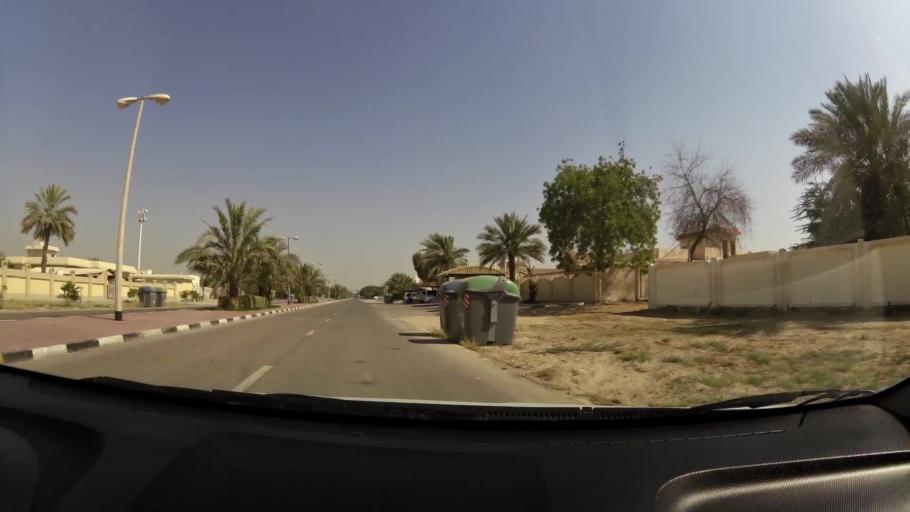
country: AE
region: Ajman
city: Ajman
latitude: 25.4196
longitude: 55.4672
